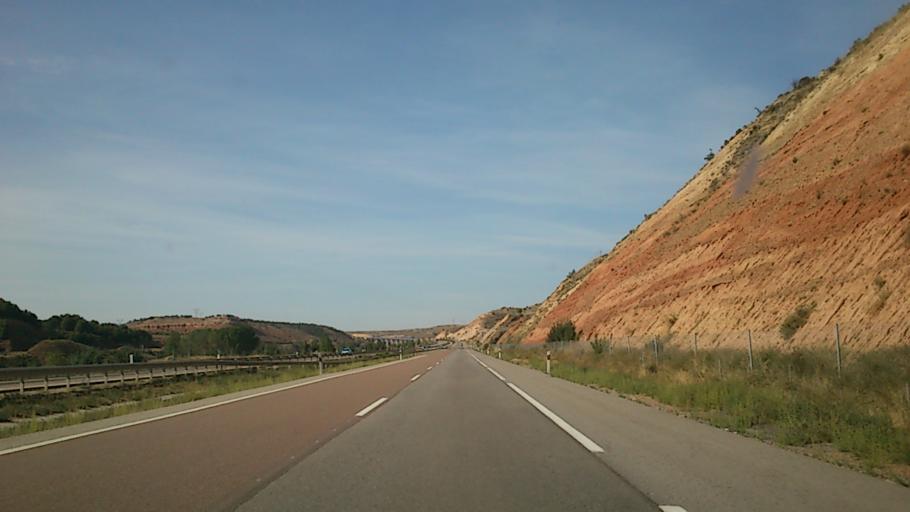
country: ES
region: Aragon
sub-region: Provincia de Teruel
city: Calamocha
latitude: 40.9759
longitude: -1.2598
